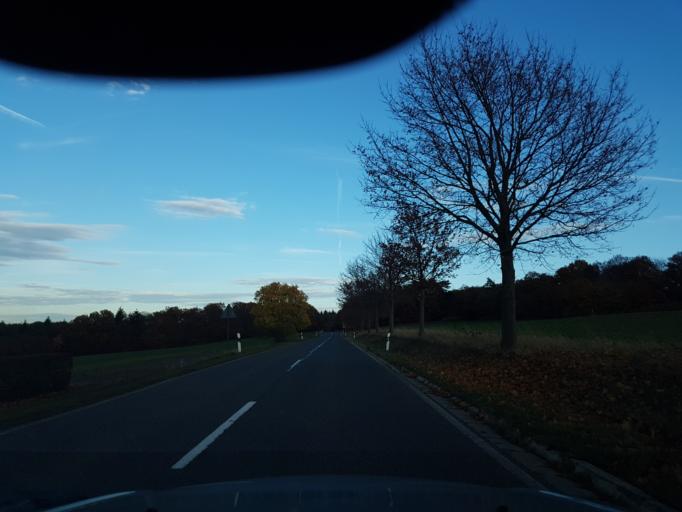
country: DE
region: Hesse
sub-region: Regierungsbezirk Darmstadt
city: Bad Schwalbach
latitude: 50.1210
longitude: 8.0185
